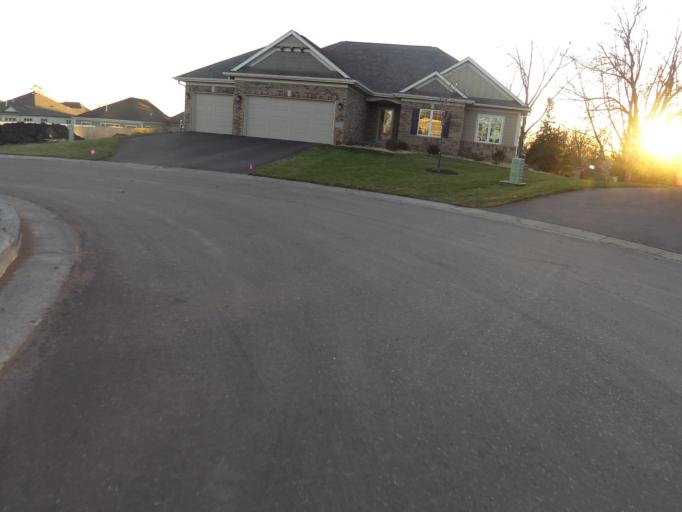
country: US
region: Wisconsin
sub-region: Saint Croix County
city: Hudson
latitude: 44.9691
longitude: -92.7305
